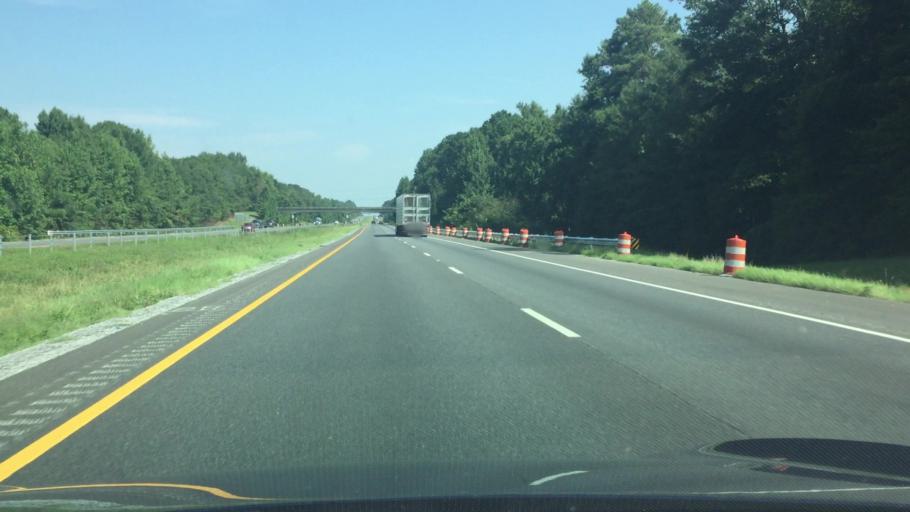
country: US
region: Alabama
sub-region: Chilton County
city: Clanton
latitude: 32.8163
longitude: -86.5854
